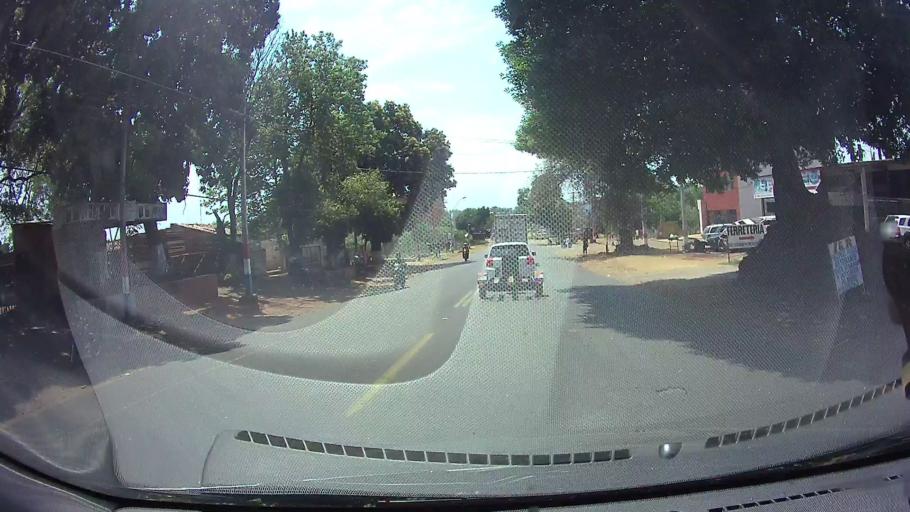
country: PY
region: Central
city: Capiata
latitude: -25.3951
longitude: -57.4672
